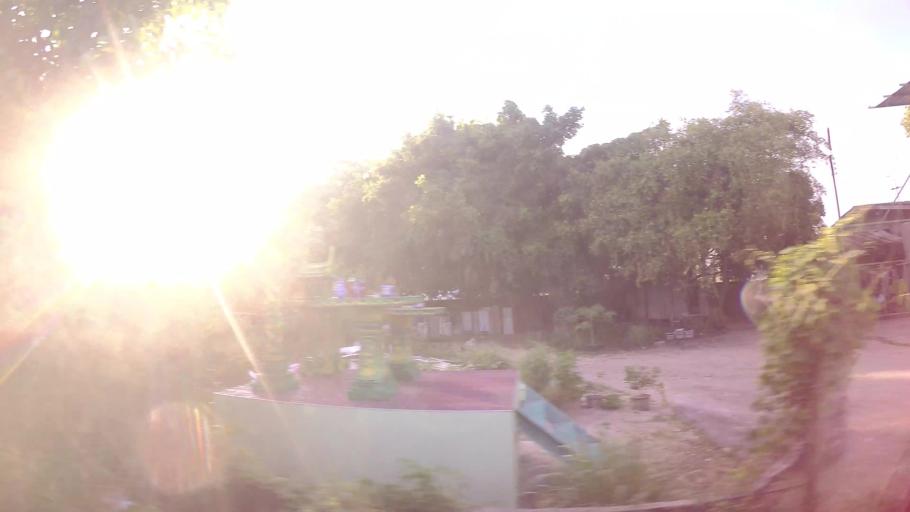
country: TH
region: Rayong
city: Rayong
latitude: 12.6864
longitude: 101.2755
